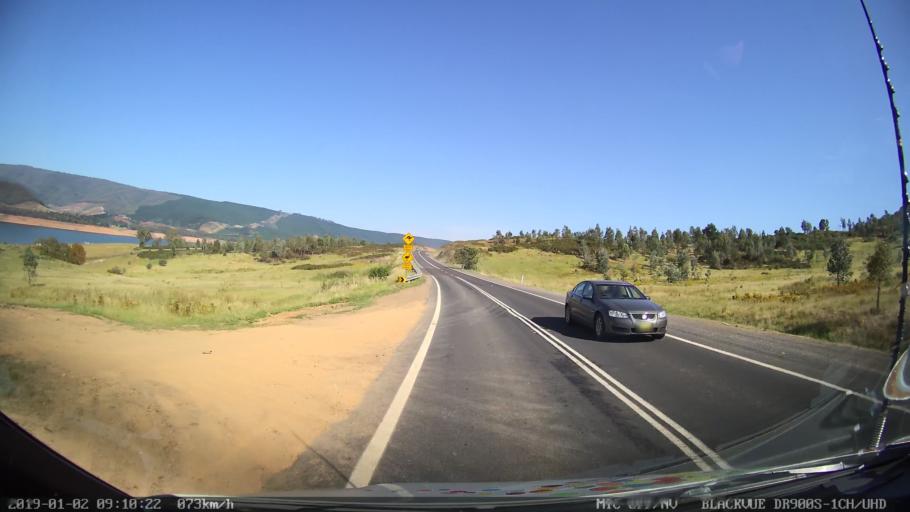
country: AU
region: New South Wales
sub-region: Tumut Shire
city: Tumut
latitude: -35.5220
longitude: 148.2708
